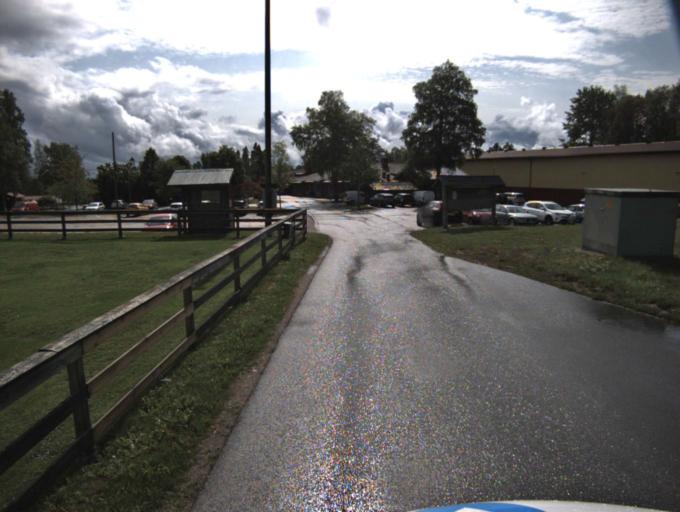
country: SE
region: Vaestra Goetaland
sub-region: Ulricehamns Kommun
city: Ulricehamn
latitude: 57.7284
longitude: 13.3091
